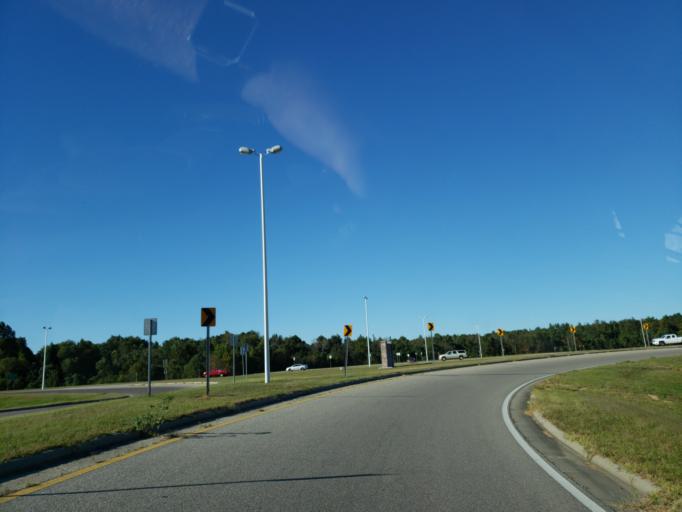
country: US
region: Mississippi
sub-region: Forrest County
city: Petal
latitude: 31.3585
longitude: -89.2748
